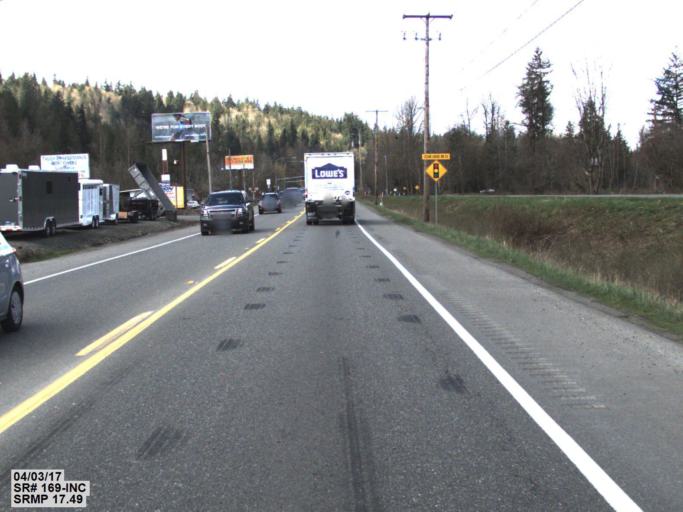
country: US
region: Washington
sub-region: King County
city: Maple Heights-Lake Desire
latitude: 47.4363
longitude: -122.0639
